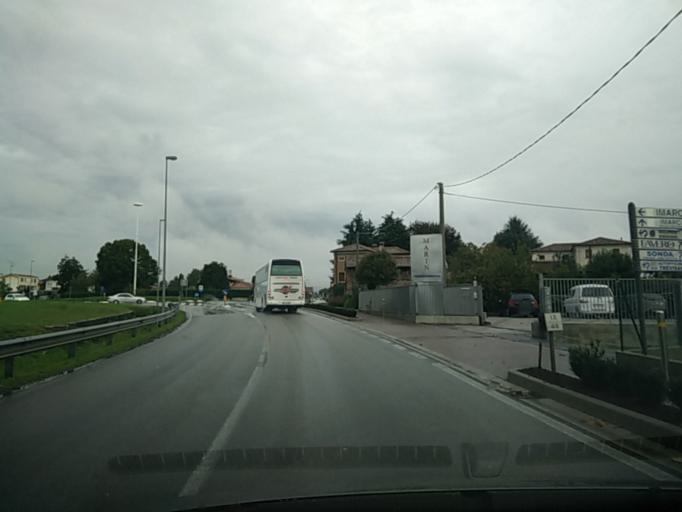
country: IT
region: Veneto
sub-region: Provincia di Vicenza
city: Rossano Veneto
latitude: 45.7135
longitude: 11.7979
